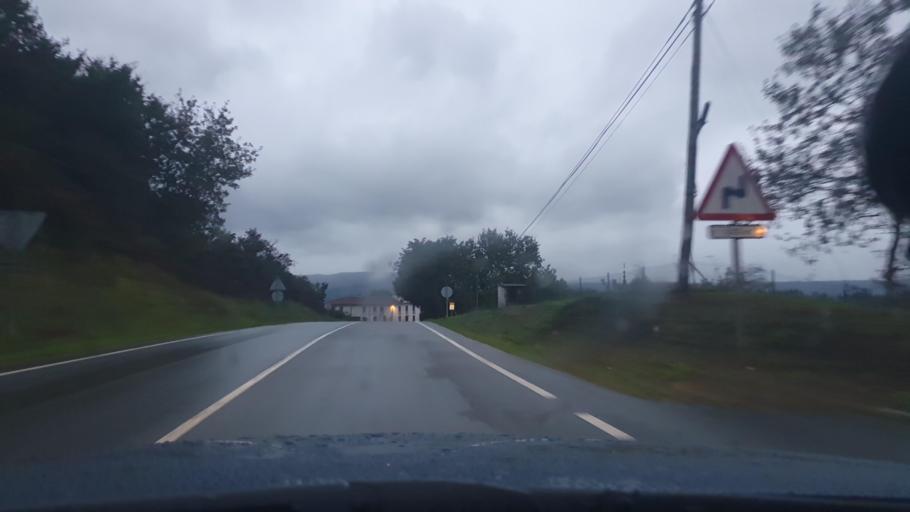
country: ES
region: Galicia
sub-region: Provincia da Coruna
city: Santiago de Compostela
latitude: 42.8416
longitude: -8.5972
